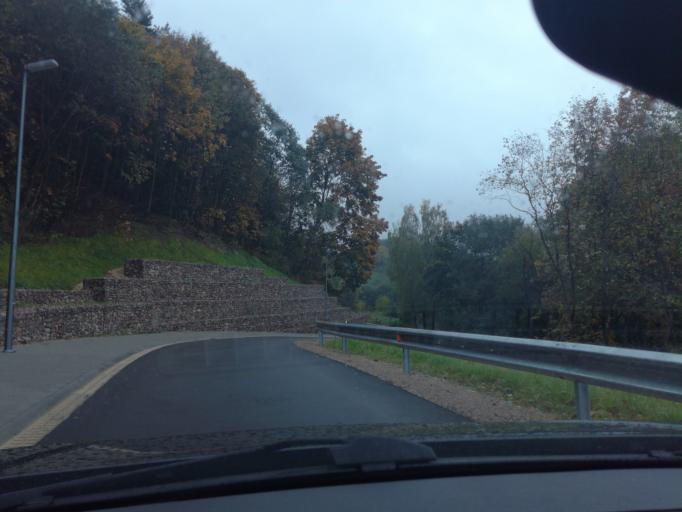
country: LT
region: Alytaus apskritis
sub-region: Alytus
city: Alytus
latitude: 54.3980
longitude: 24.0746
